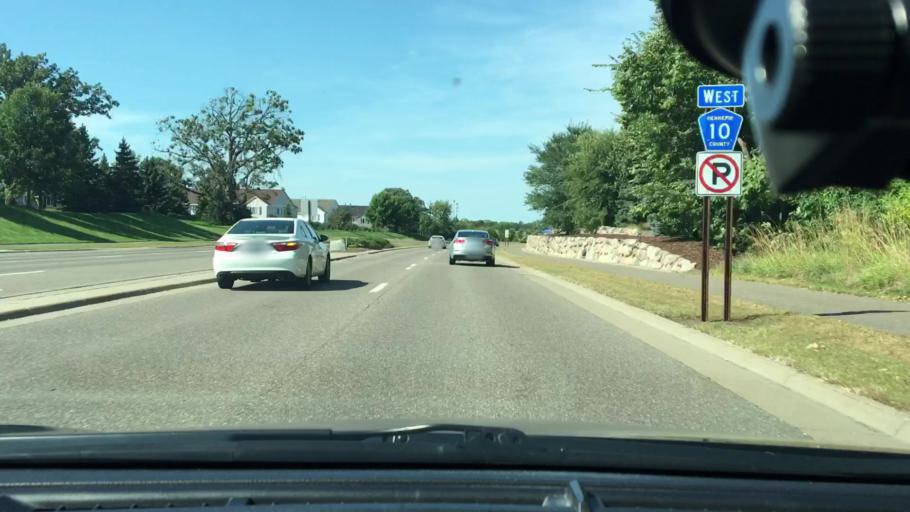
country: US
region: Minnesota
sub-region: Hennepin County
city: Corcoran
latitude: 45.0822
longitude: -93.5081
